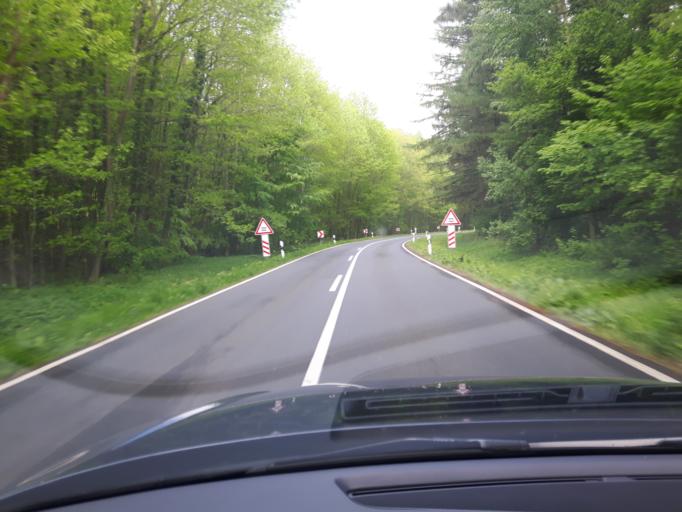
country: DE
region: Mecklenburg-Vorpommern
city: Trinwillershagen
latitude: 54.2660
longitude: 12.7144
